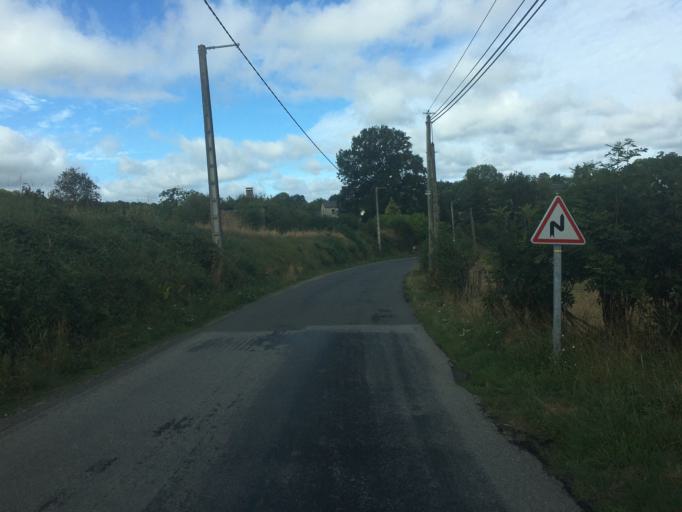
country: FR
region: Limousin
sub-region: Departement de la Correze
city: Bort-les-Orgues
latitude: 45.4133
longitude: 2.4335
